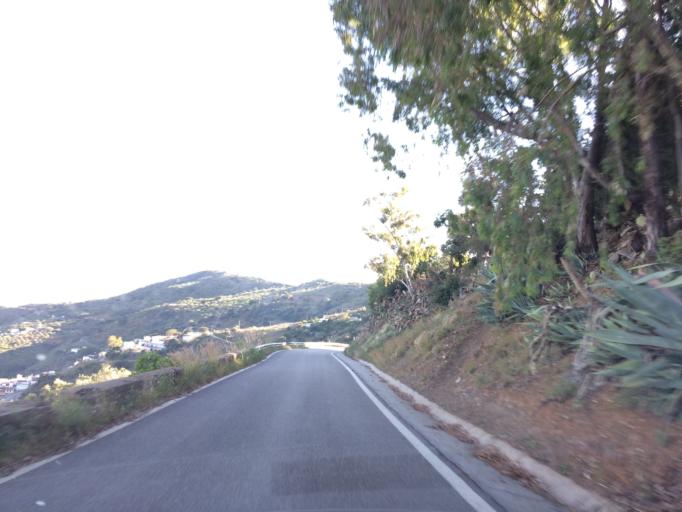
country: ES
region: Andalusia
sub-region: Provincia de Malaga
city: Totalan
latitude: 36.7783
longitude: -4.3175
